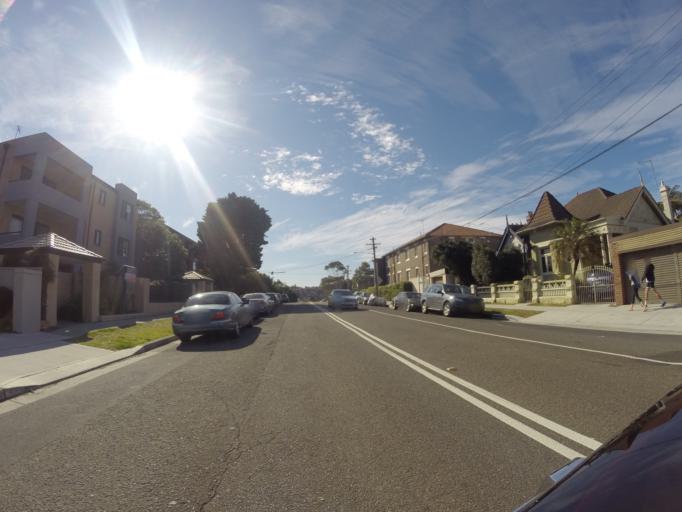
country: AU
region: New South Wales
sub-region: Randwick
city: Coogee
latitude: -33.9217
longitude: 151.2517
